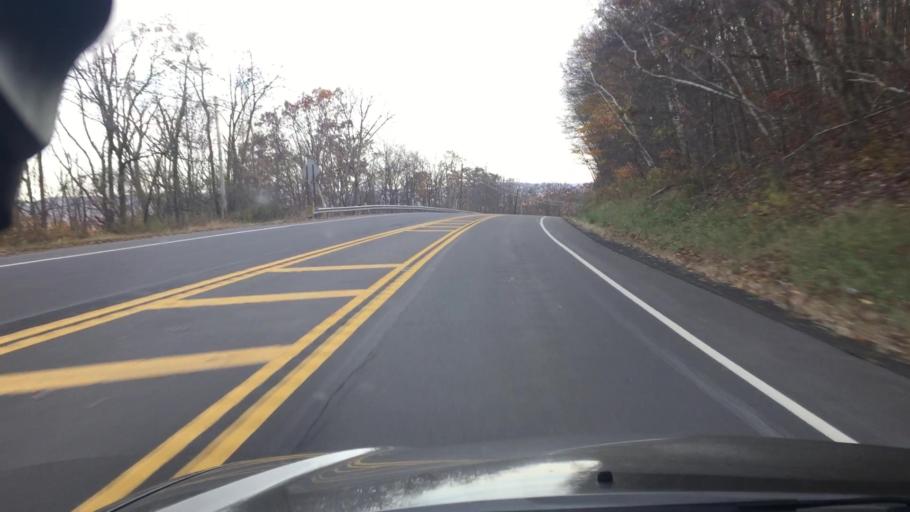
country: US
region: Pennsylvania
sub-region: Luzerne County
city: Freeland
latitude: 41.0812
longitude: -75.9550
